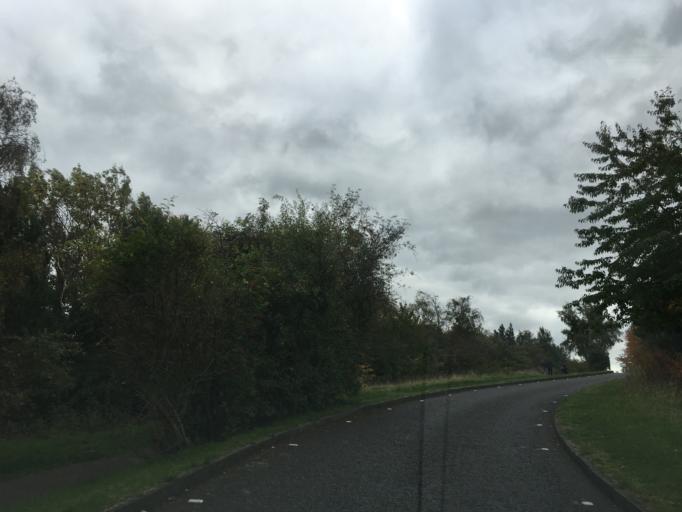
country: GB
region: Scotland
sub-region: West Lothian
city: Seafield
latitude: 55.9513
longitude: -3.1510
